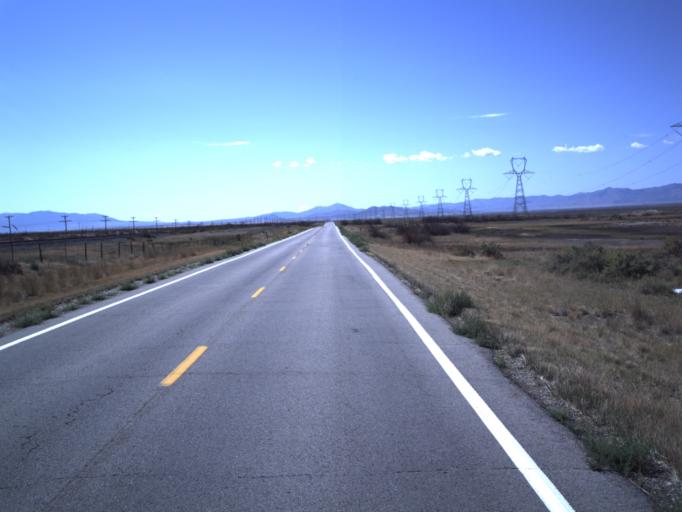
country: US
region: Utah
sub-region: Tooele County
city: Tooele
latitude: 40.3282
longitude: -112.4079
